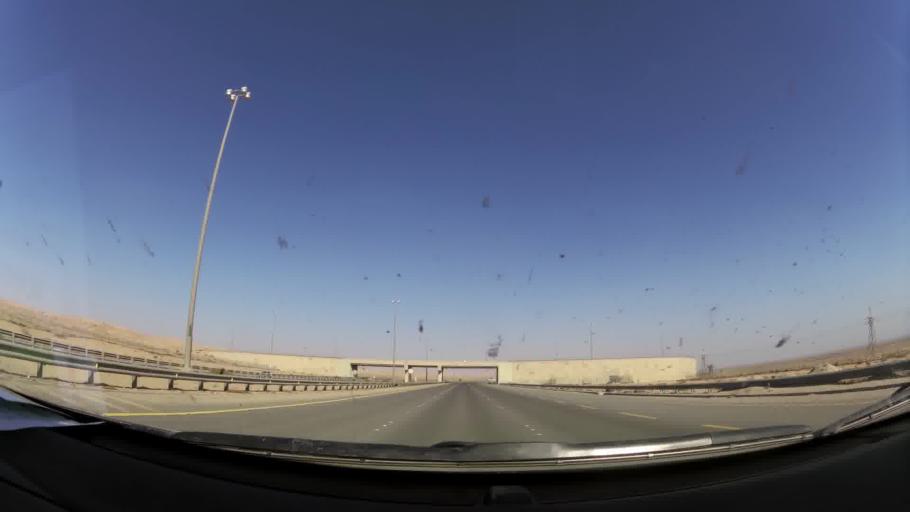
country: KW
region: Al Asimah
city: Kuwait City
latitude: 29.5264
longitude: 47.8204
